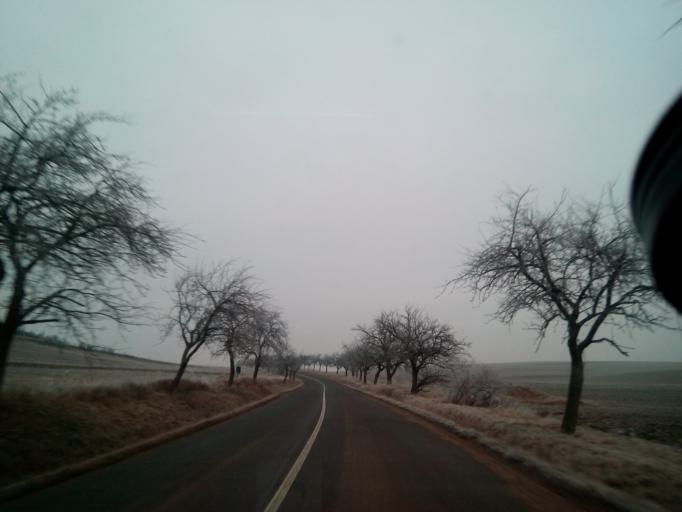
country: SK
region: Presovsky
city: Lubica
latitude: 48.9800
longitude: 20.4184
